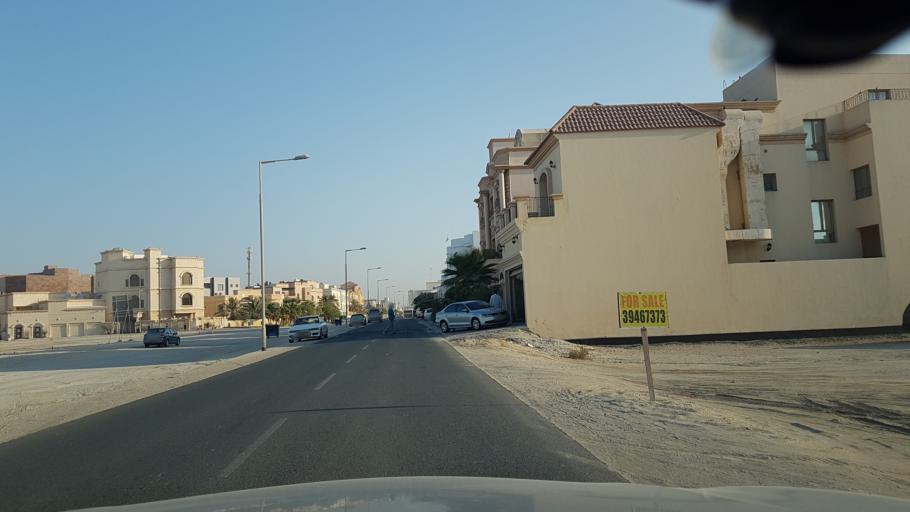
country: BH
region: Muharraq
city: Al Muharraq
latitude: 26.2811
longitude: 50.6030
